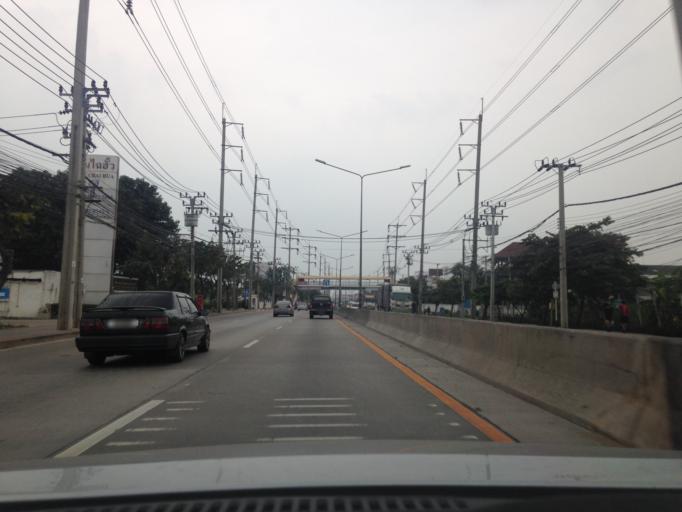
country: TH
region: Bangkok
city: Lat Krabang
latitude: 13.7437
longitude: 100.7465
